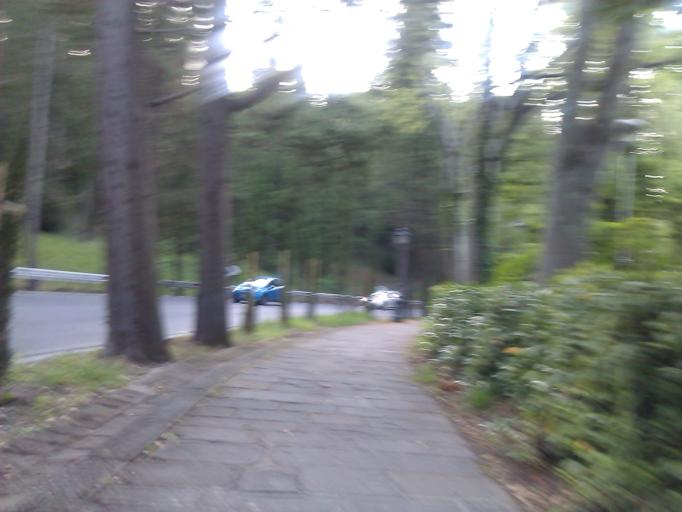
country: IT
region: Tuscany
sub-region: Province of Florence
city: Florence
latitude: 43.7567
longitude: 11.2685
